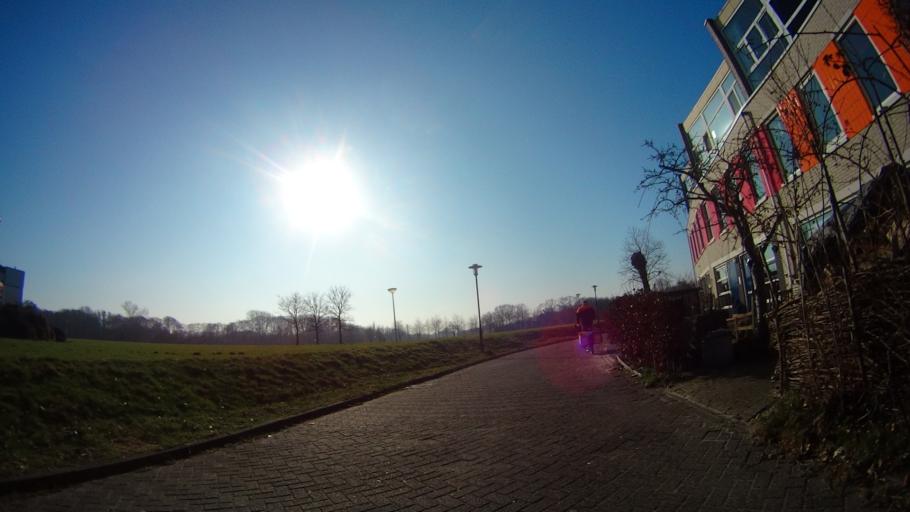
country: NL
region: Utrecht
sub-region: Gemeente Amersfoort
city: Hoogland
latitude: 52.1836
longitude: 5.3866
